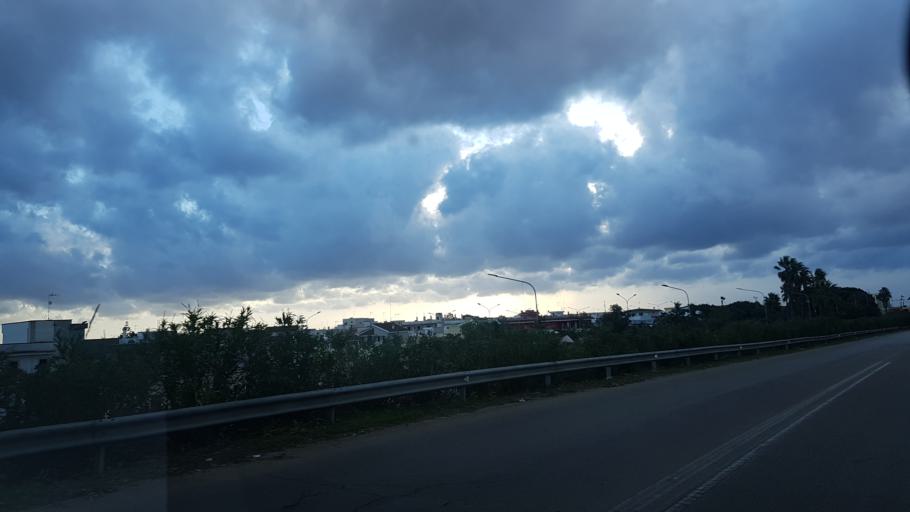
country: IT
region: Apulia
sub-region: Provincia di Brindisi
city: San Pietro Vernotico
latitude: 40.4989
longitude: 17.9969
